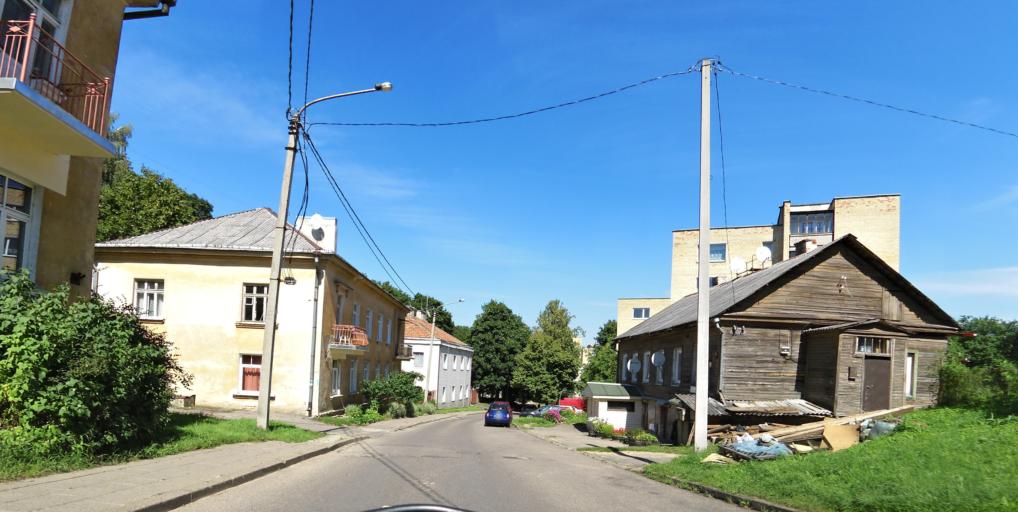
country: LT
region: Vilnius County
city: Naujamiestis
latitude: 54.6664
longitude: 25.2892
